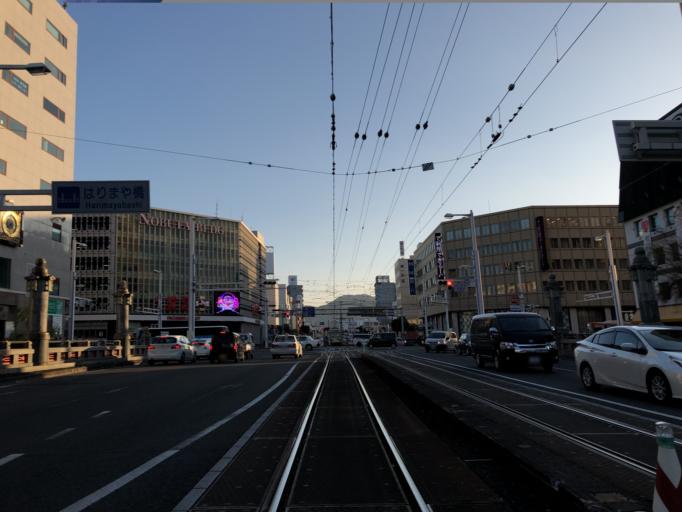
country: JP
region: Kochi
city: Kochi-shi
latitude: 33.5601
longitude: 133.5427
